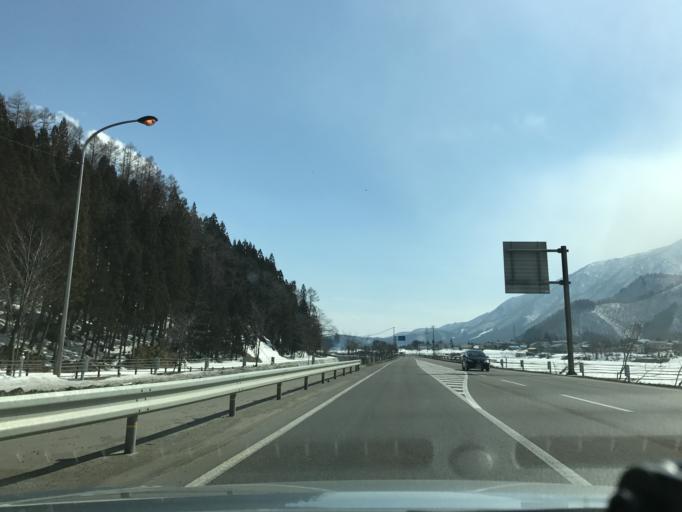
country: JP
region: Nagano
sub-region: Kitaazumi Gun
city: Hakuba
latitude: 36.6674
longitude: 137.8517
